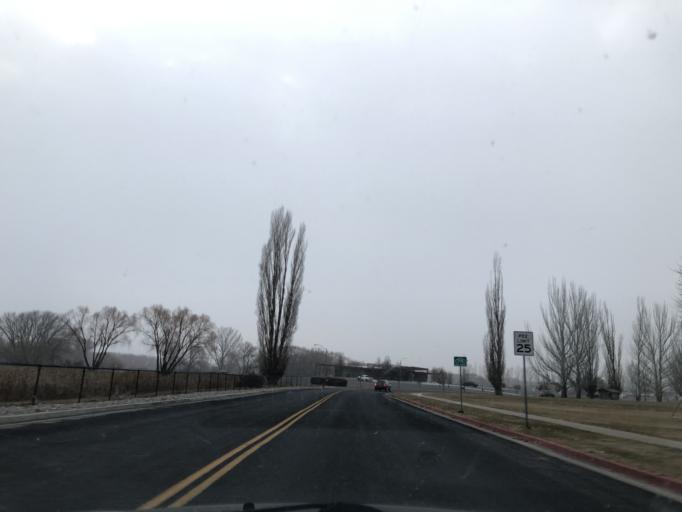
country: US
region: Utah
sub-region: Cache County
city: Logan
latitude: 41.7140
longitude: -111.8475
